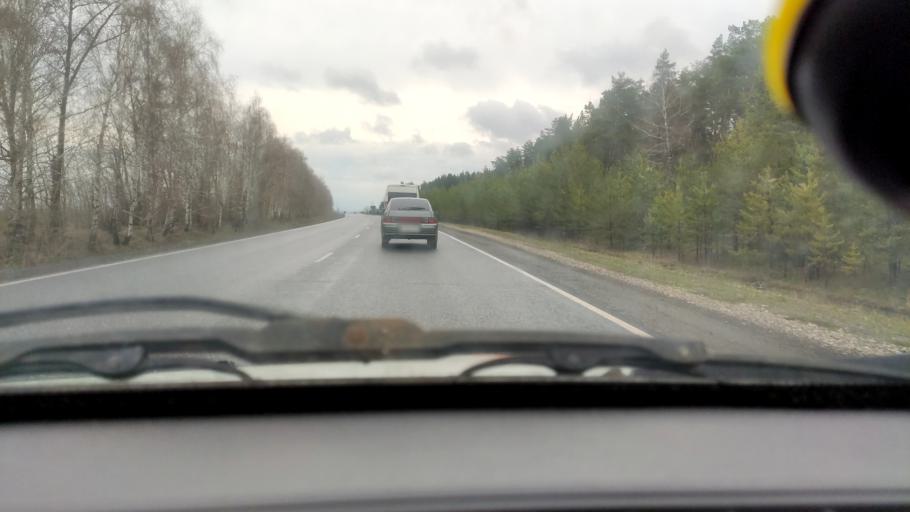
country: RU
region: Samara
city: Povolzhskiy
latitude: 53.6255
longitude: 49.6511
